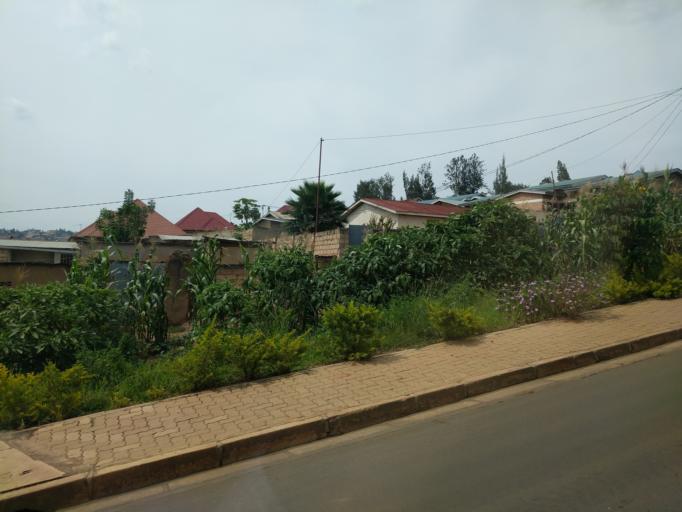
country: RW
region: Kigali
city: Kigali
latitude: -1.9738
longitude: 30.1209
